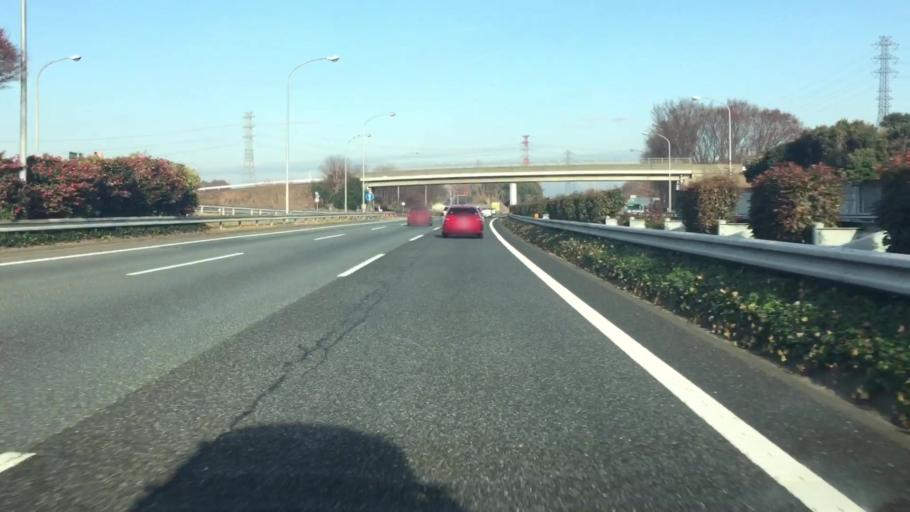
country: JP
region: Saitama
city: Yorii
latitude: 36.1720
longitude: 139.1943
